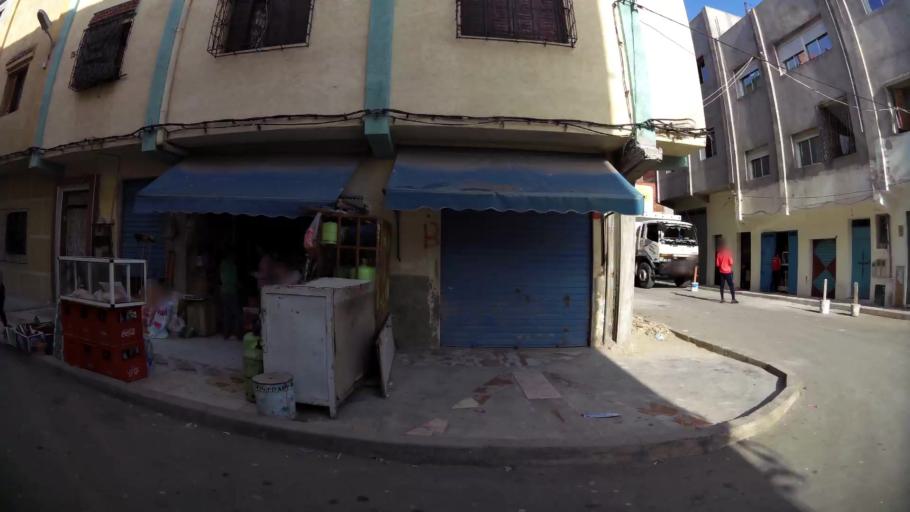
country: MA
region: Tanger-Tetouan
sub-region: Tetouan
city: Martil
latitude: 35.6116
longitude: -5.2744
